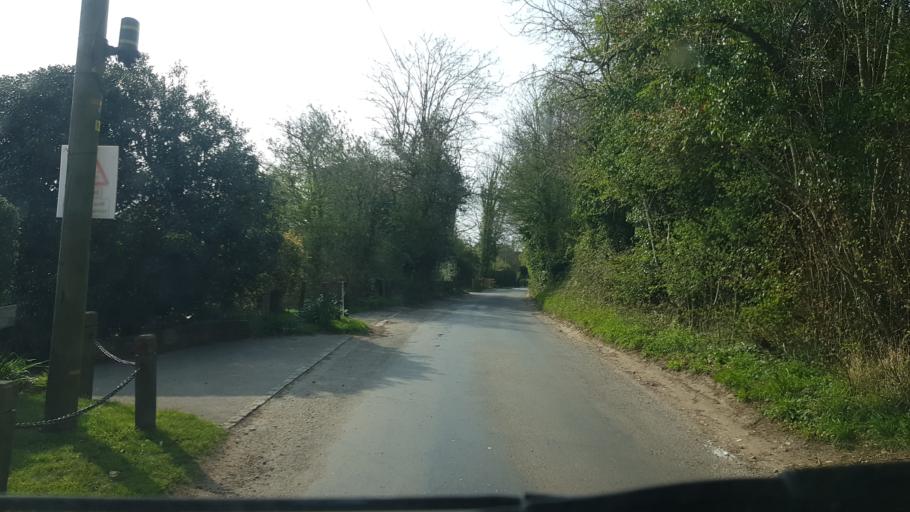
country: GB
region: England
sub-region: Surrey
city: Chilworth
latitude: 51.2315
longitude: -0.5289
